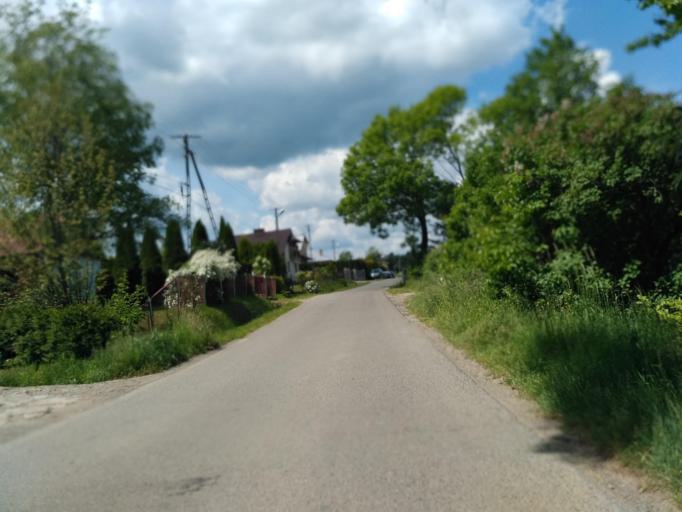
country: PL
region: Subcarpathian Voivodeship
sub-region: Powiat krosnienski
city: Dukla
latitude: 49.5535
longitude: 21.6649
